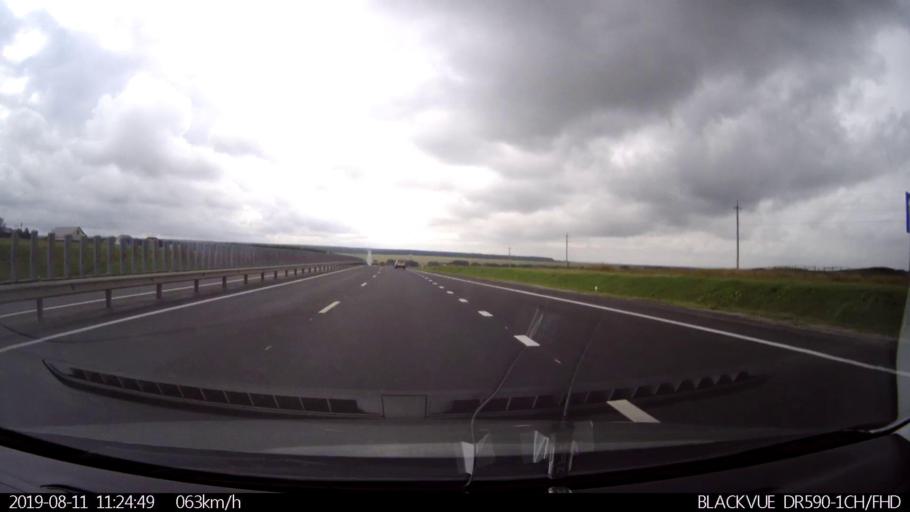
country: RU
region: Ulyanovsk
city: Krasnyy Gulyay
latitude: 54.1240
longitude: 48.2403
